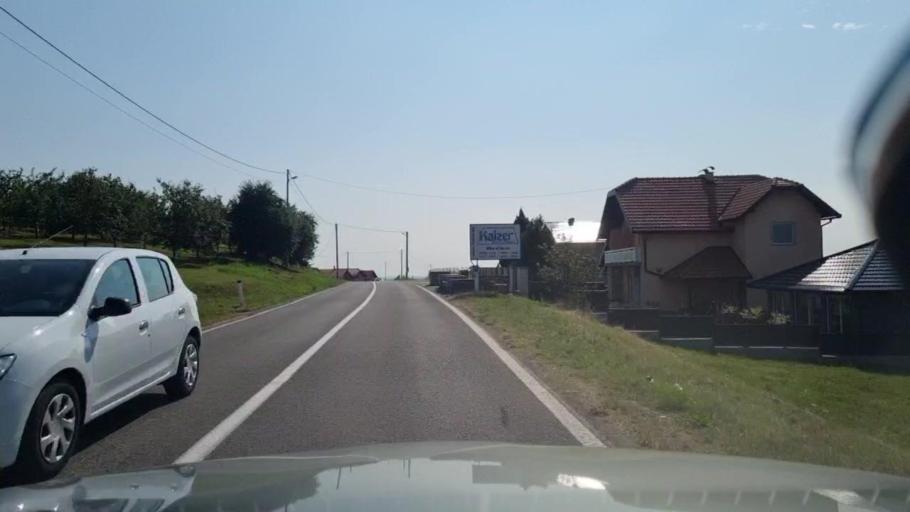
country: BA
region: Federation of Bosnia and Herzegovina
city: Mionica
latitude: 44.8696
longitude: 18.4849
